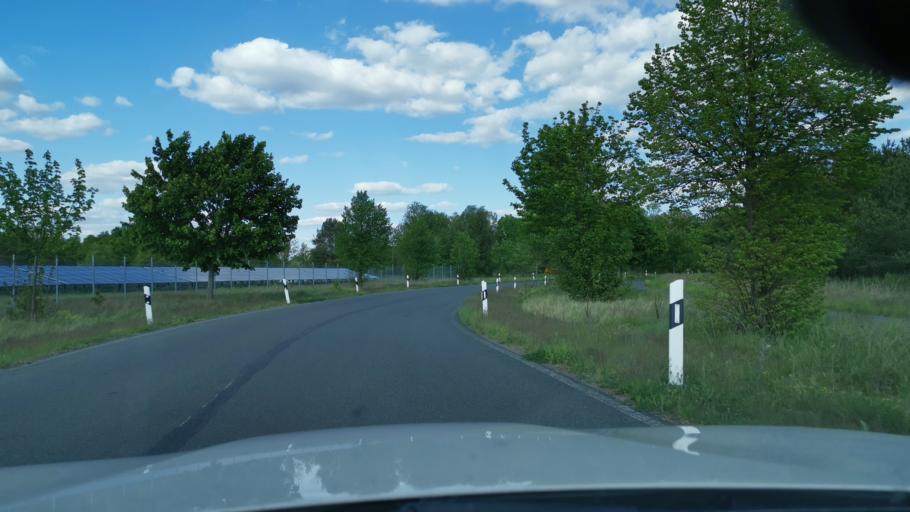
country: DE
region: Brandenburg
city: Niedergorsdorf
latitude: 51.9929
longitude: 13.0037
